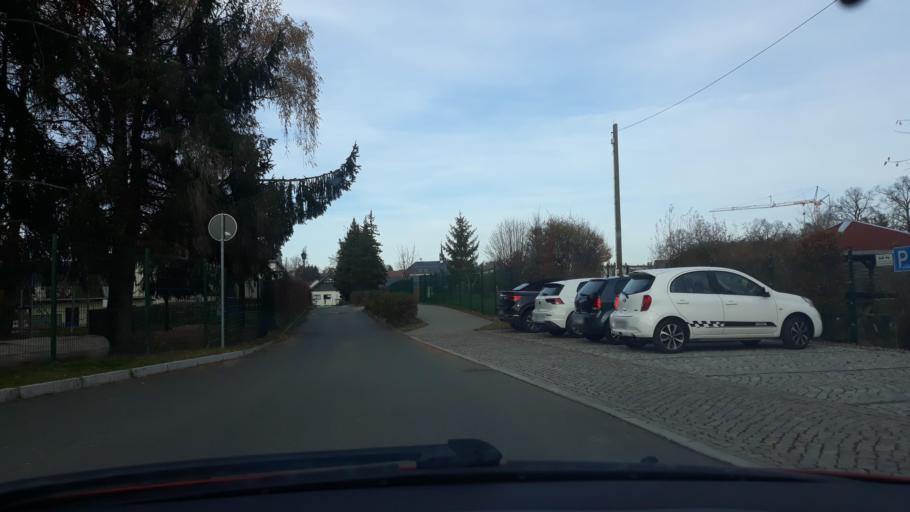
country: DE
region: Saxony
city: Wilkau-Hasslau
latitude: 50.6808
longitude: 12.5479
